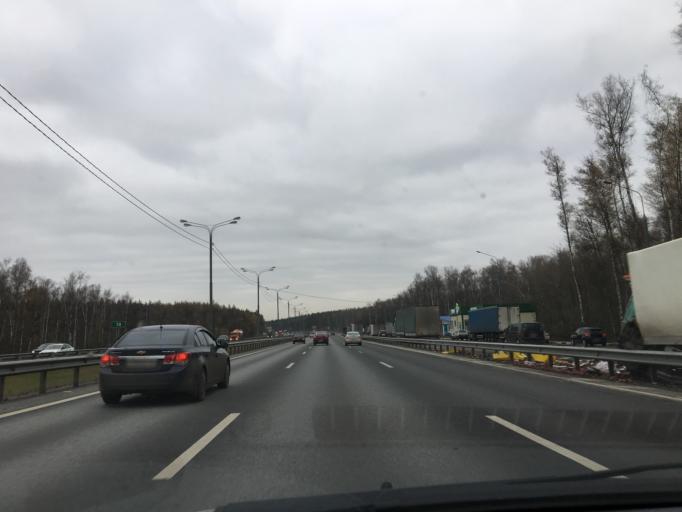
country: RU
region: Moskovskaya
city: Vostryakovo
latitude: 55.4328
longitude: 37.7986
